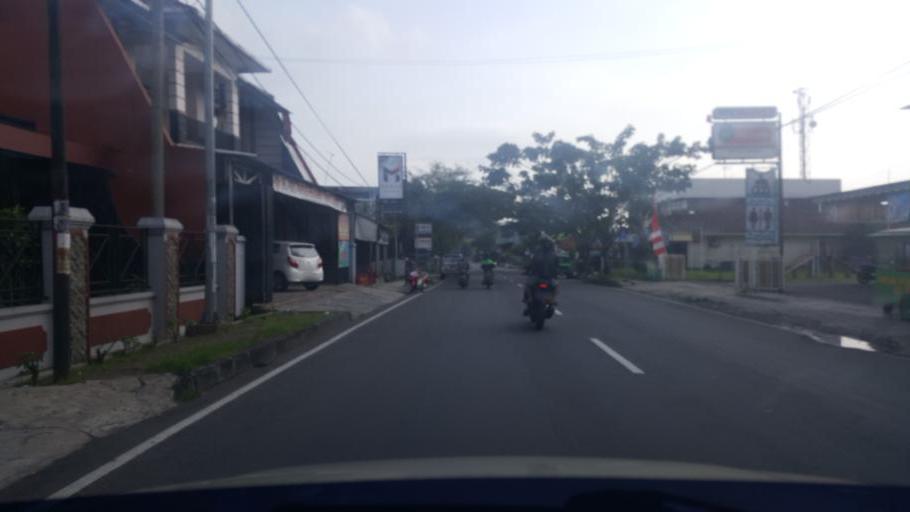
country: ID
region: West Java
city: Cibogor
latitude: -7.3170
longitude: 108.2282
